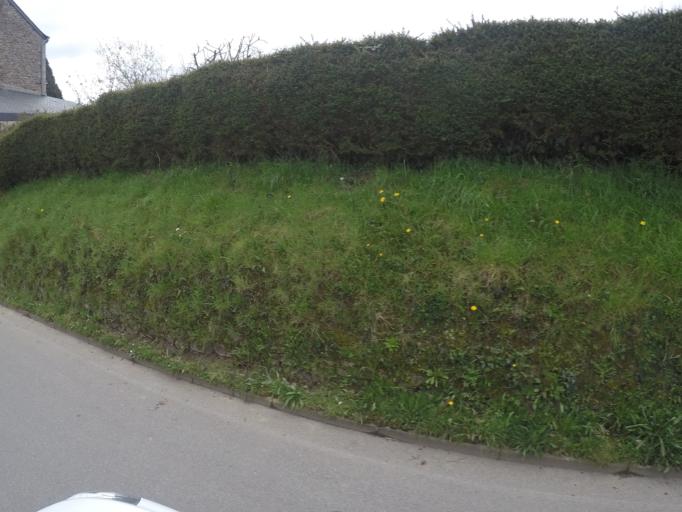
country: FR
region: Brittany
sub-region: Departement des Cotes-d'Armor
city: Plouha
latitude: 48.6728
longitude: -2.9292
